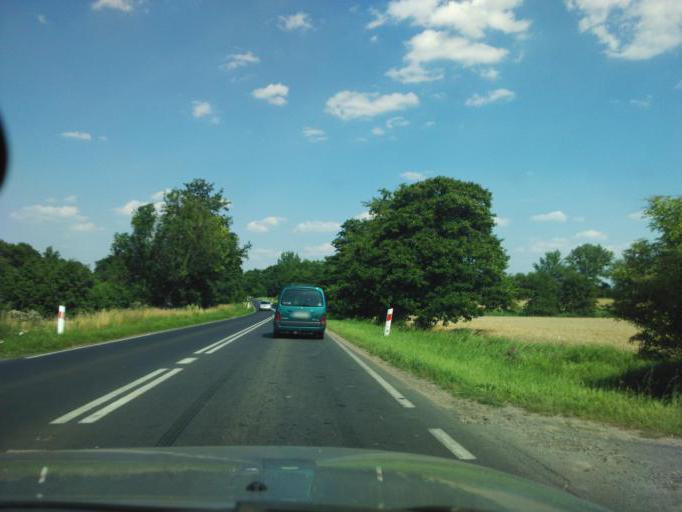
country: PL
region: West Pomeranian Voivodeship
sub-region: Powiat pyrzycki
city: Pyrzyce
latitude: 53.1323
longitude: 14.8701
